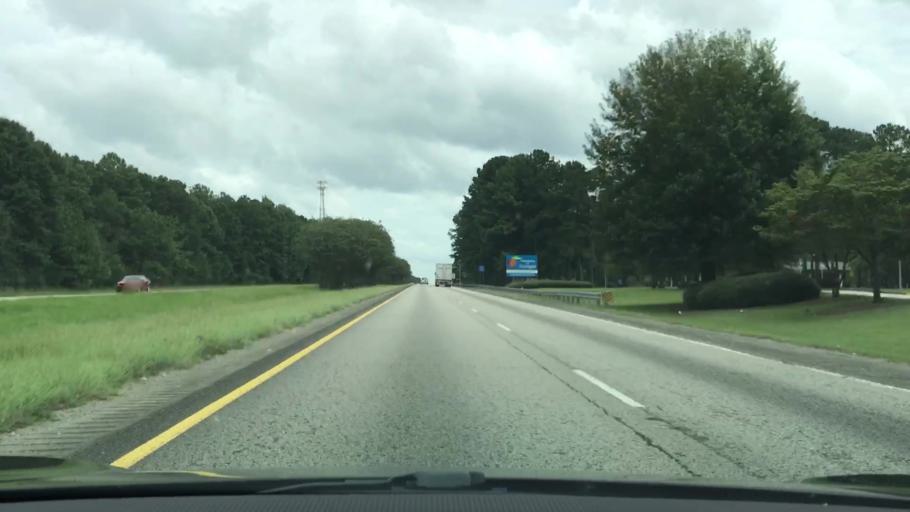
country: US
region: Alabama
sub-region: Chambers County
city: Lanett
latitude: 32.8586
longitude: -85.1745
